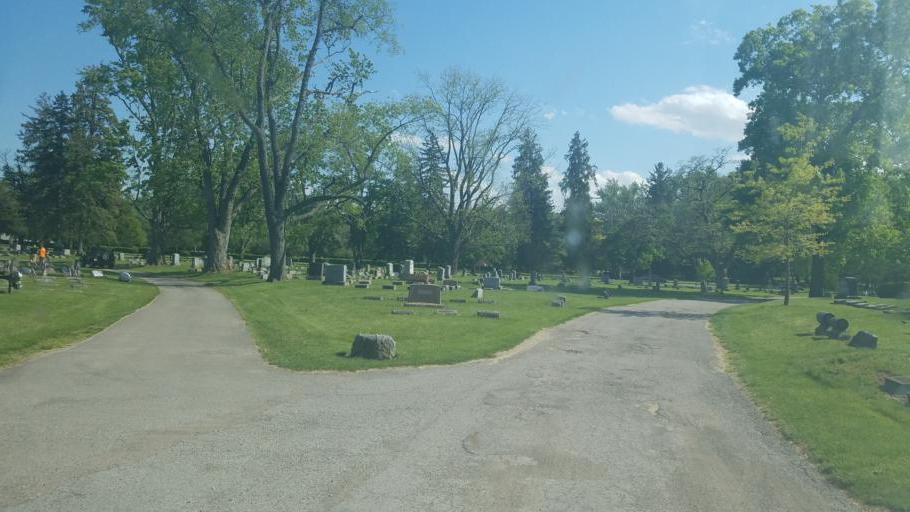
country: US
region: Ohio
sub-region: Marion County
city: Marion
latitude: 40.5756
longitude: -83.1210
